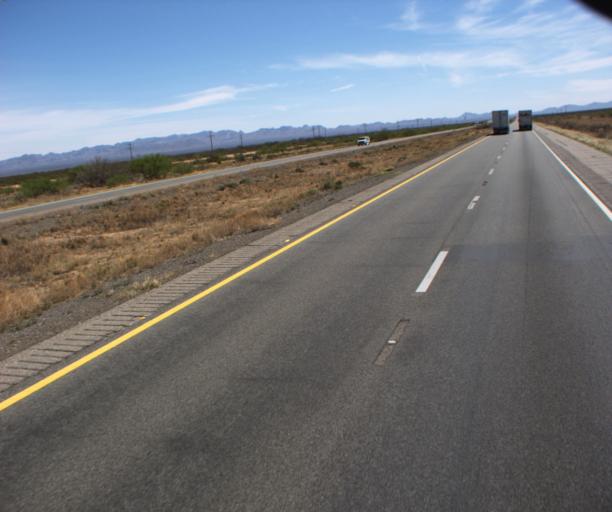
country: US
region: Arizona
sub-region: Cochise County
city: Willcox
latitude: 32.2992
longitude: -109.3629
